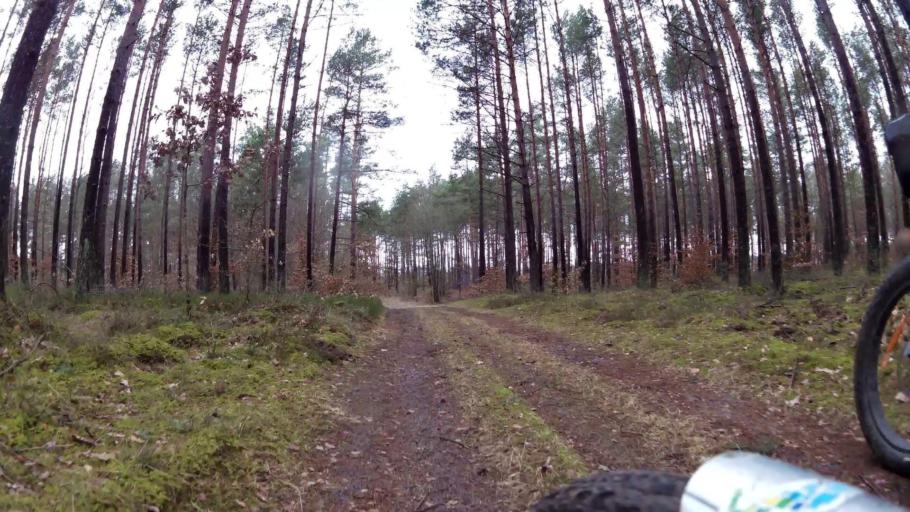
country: PL
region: Pomeranian Voivodeship
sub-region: Powiat bytowski
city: Kolczyglowy
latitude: 54.2399
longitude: 17.2511
